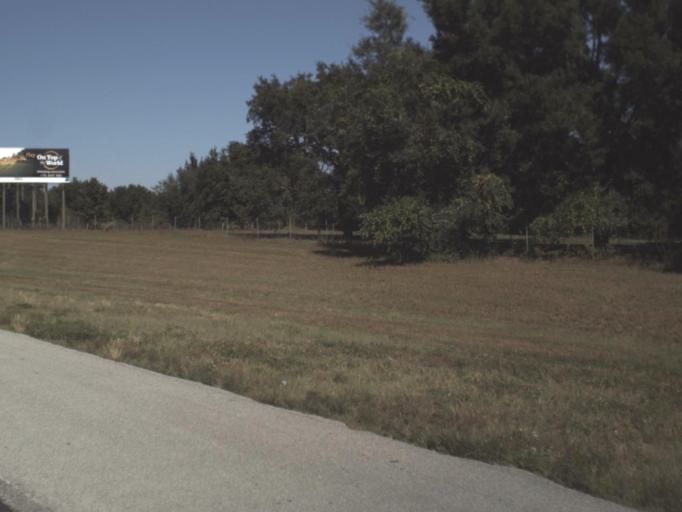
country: US
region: Florida
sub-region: Lake County
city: Hawthorne
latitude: 28.6955
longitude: -81.8754
